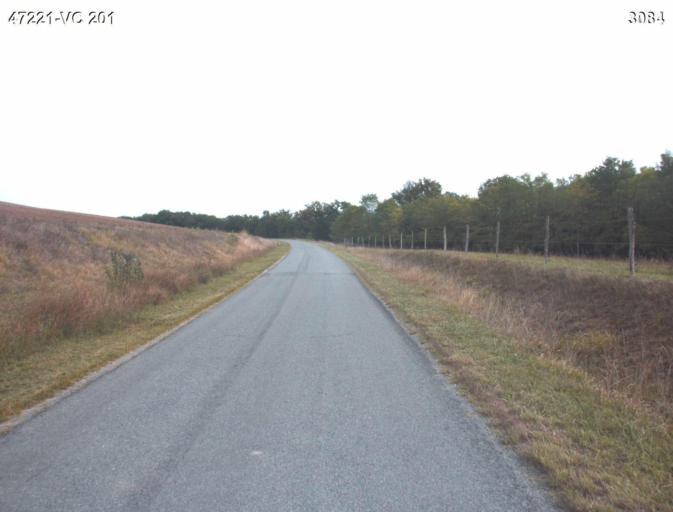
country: FR
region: Aquitaine
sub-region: Departement du Lot-et-Garonne
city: Mezin
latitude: 44.1090
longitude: 0.2558
